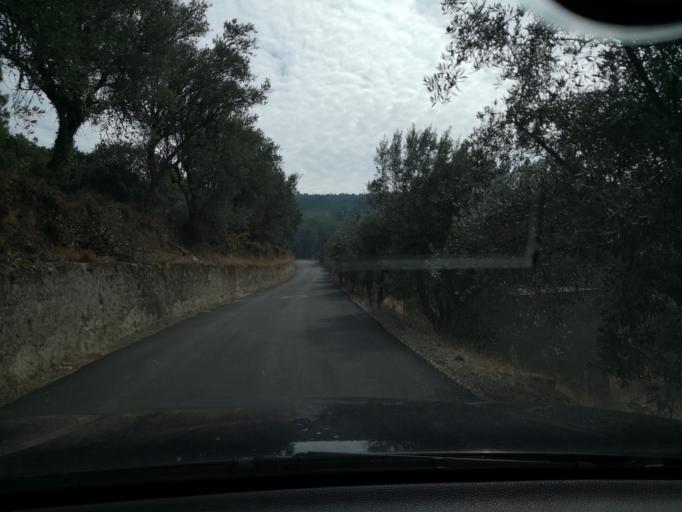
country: PT
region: Vila Real
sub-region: Sabrosa
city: Vilela
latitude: 41.2165
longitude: -7.6855
